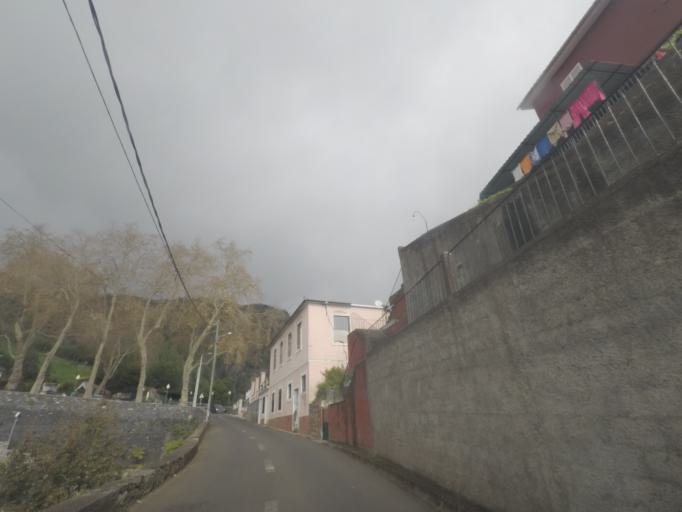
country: PT
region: Madeira
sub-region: Funchal
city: Nossa Senhora do Monte
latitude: 32.6755
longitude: -16.8991
